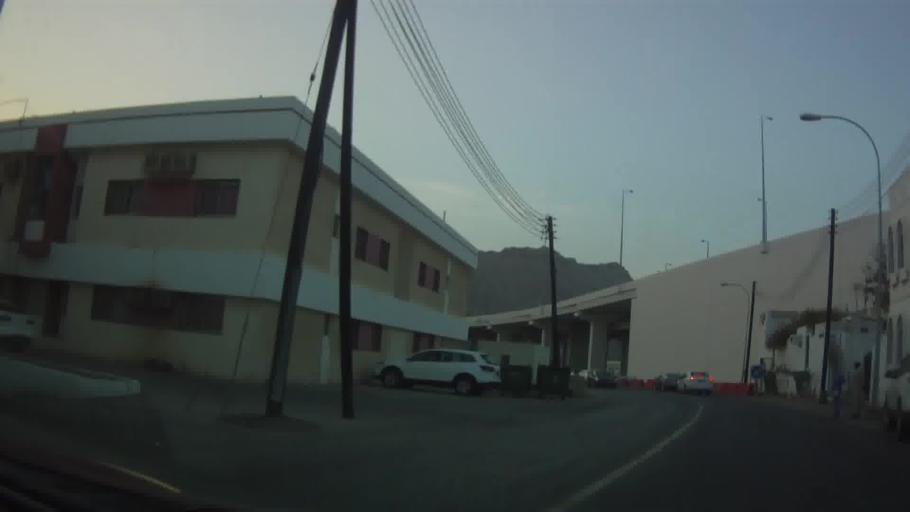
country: OM
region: Muhafazat Masqat
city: Muscat
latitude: 23.6181
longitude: 58.5413
